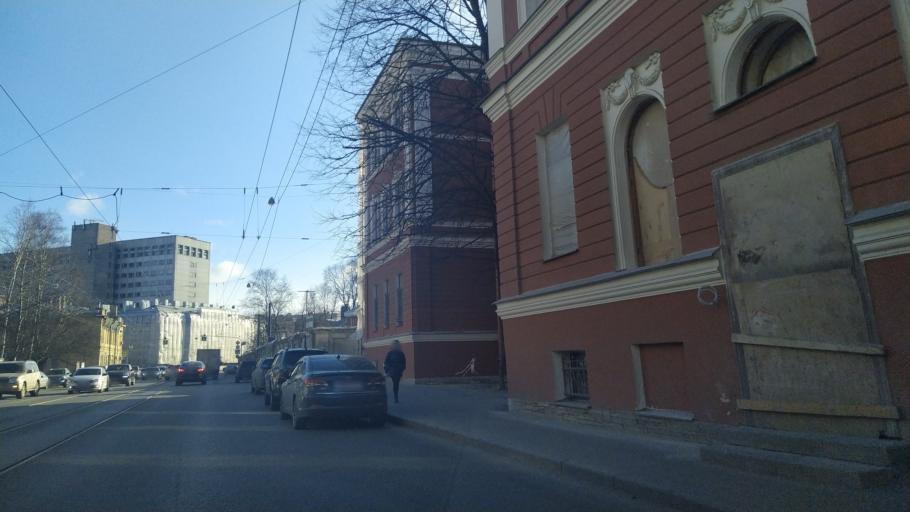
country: RU
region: Leningrad
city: Finlyandskiy
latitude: 59.9615
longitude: 30.3528
